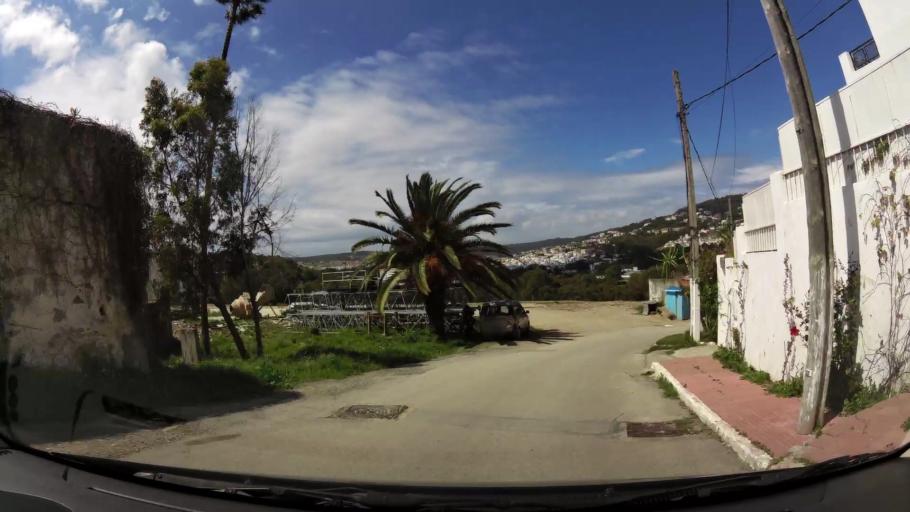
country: MA
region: Tanger-Tetouan
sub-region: Tanger-Assilah
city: Tangier
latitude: 35.7780
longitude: -5.8373
